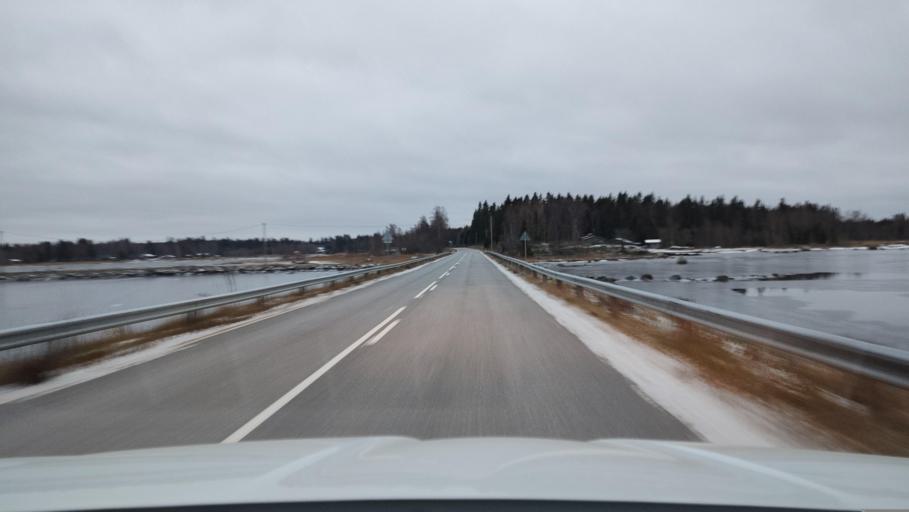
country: FI
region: Ostrobothnia
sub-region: Vaasa
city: Replot
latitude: 63.2725
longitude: 21.3439
